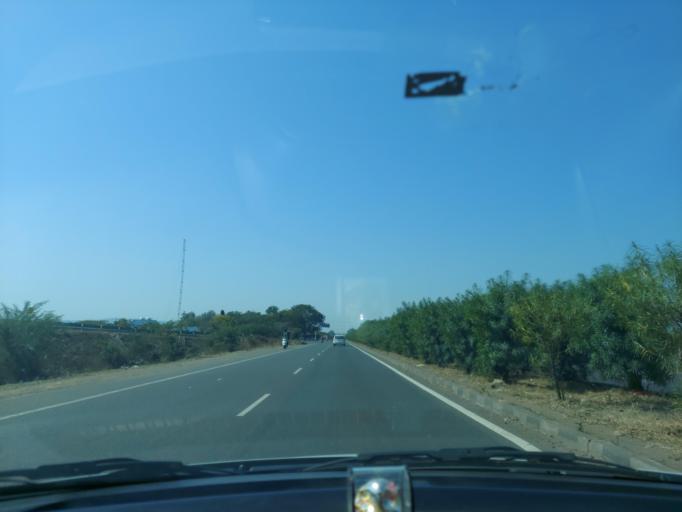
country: IN
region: Madhya Pradesh
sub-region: Indore
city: Manpur
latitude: 22.4272
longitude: 75.6122
